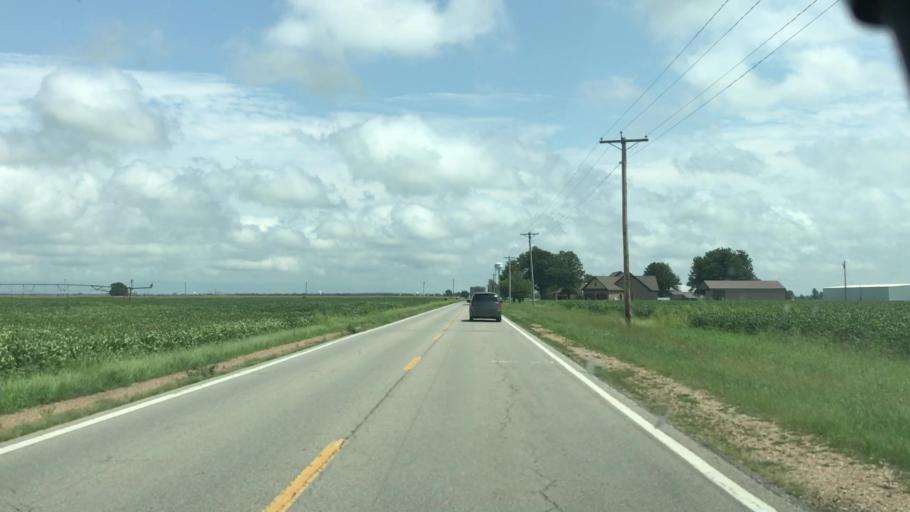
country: US
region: Missouri
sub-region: Pemiscot County
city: Hayti
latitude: 36.1760
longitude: -89.7287
